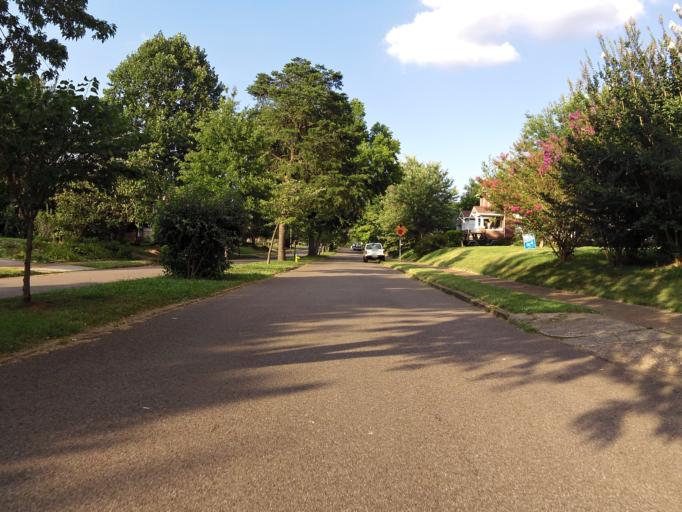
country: US
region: Tennessee
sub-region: Knox County
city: Knoxville
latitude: 36.0074
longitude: -83.9214
